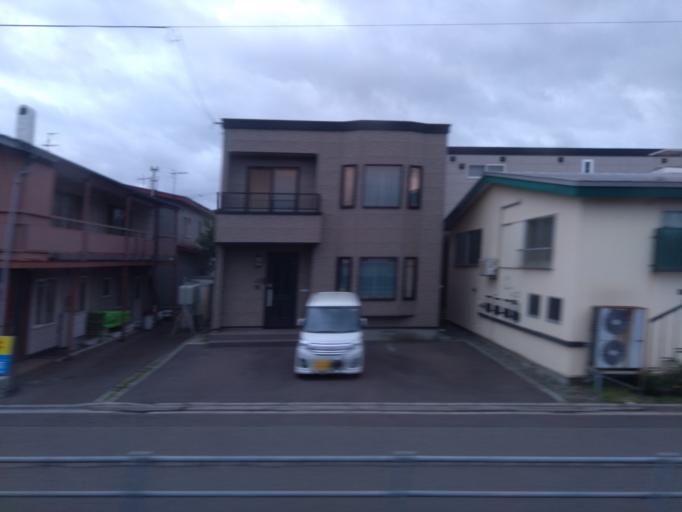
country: JP
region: Hokkaido
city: Hakodate
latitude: 41.7924
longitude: 140.7312
